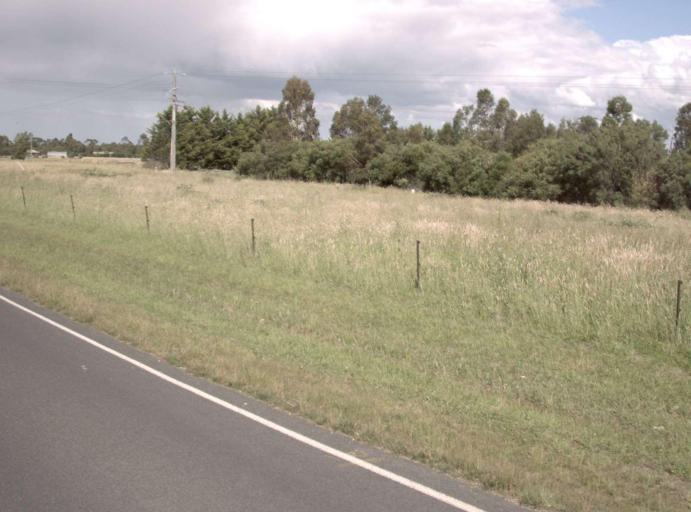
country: AU
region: Victoria
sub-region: Latrobe
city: Traralgon
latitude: -38.1310
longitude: 146.5575
